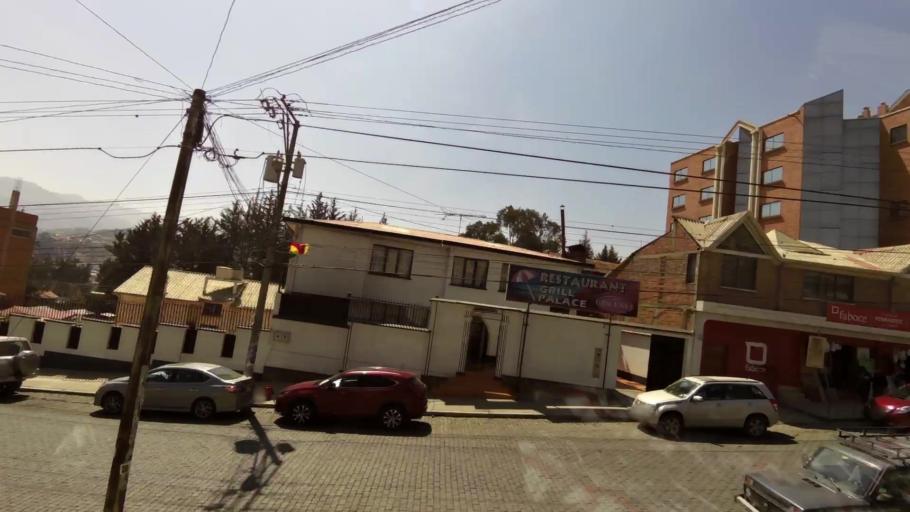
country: BO
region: La Paz
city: La Paz
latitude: -16.5402
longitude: -68.0700
